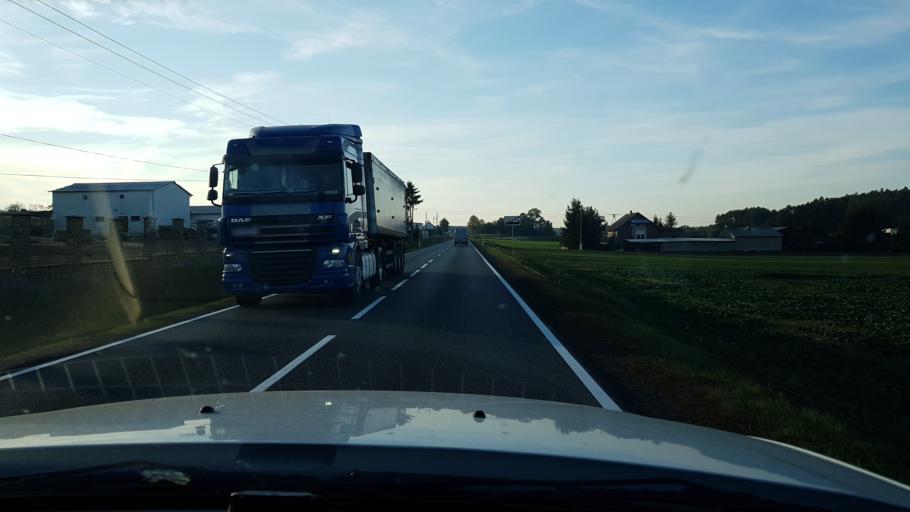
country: PL
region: West Pomeranian Voivodeship
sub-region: Powiat gryfinski
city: Chojna
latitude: 52.9630
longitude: 14.4107
